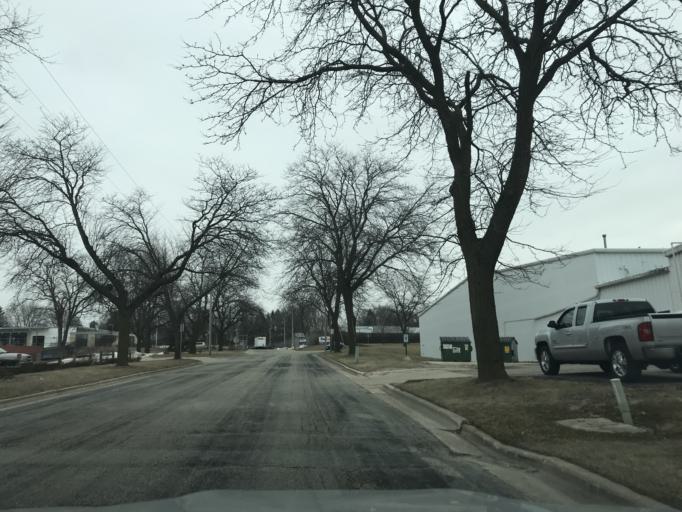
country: US
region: Wisconsin
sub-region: Dane County
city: Monona
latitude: 43.0933
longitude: -89.3102
